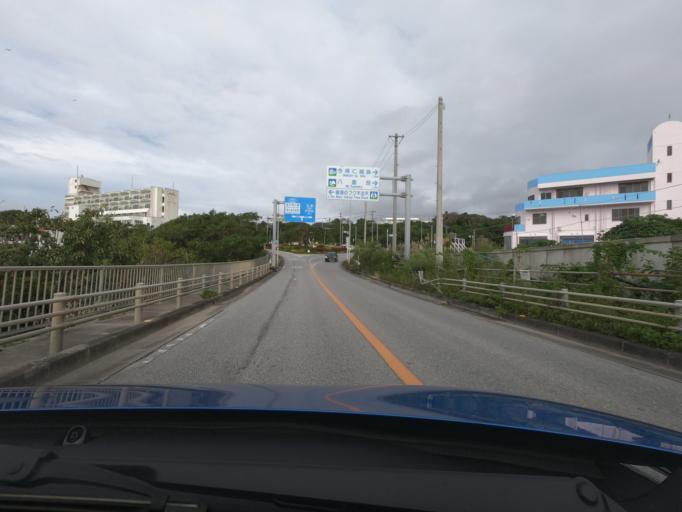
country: JP
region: Okinawa
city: Nago
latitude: 26.6623
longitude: 127.8906
